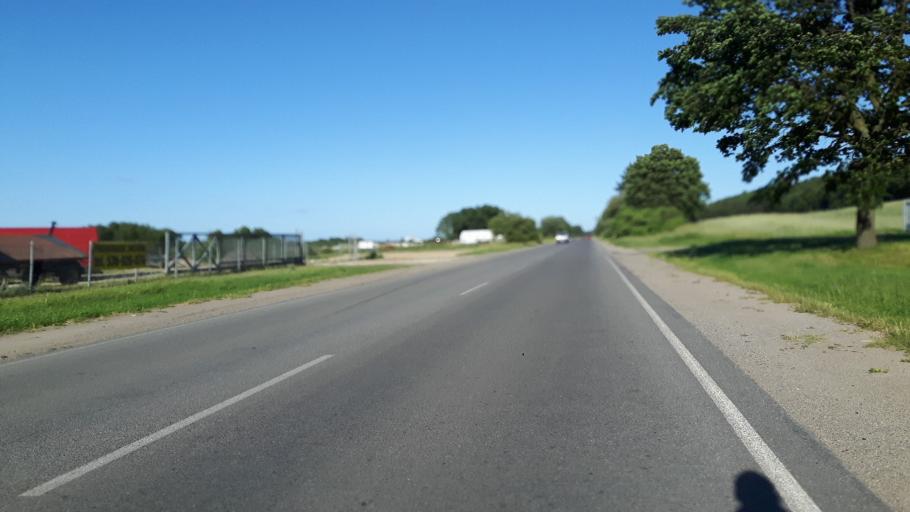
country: PL
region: Pomeranian Voivodeship
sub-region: Powiat pucki
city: Mrzezino
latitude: 54.6051
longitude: 18.4337
